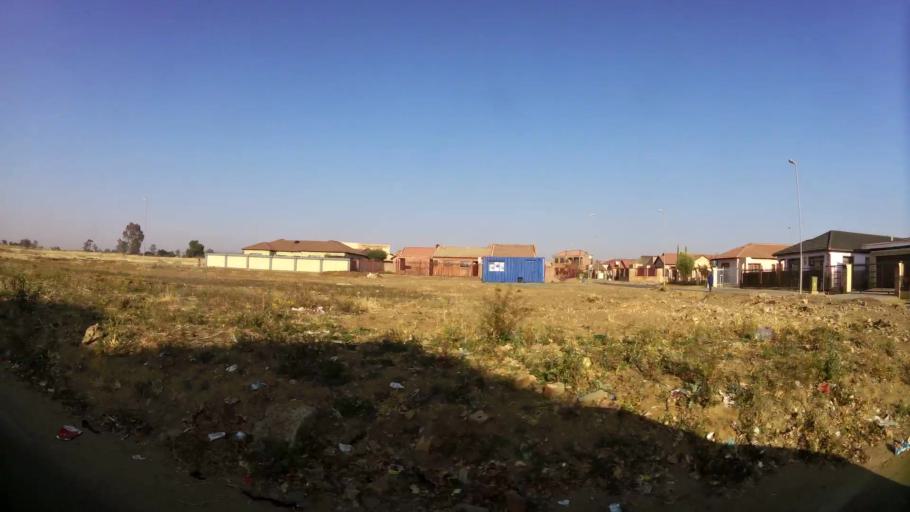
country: ZA
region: Orange Free State
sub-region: Mangaung Metropolitan Municipality
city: Bloemfontein
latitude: -29.1582
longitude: 26.2110
